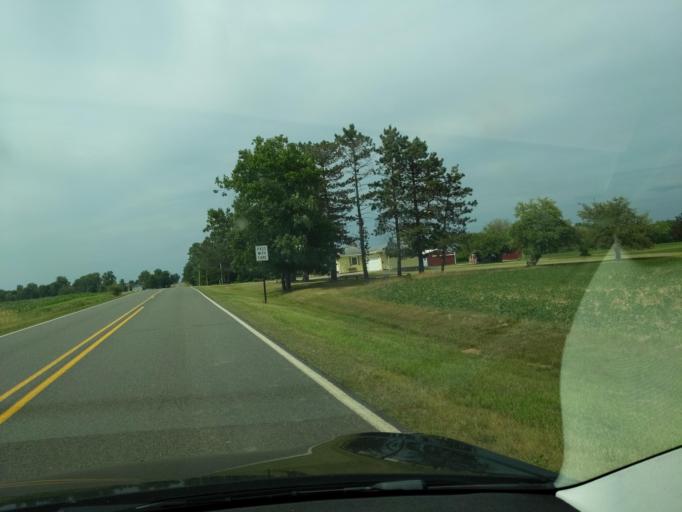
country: US
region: Michigan
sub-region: Clinton County
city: DeWitt
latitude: 42.8954
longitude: -84.6022
